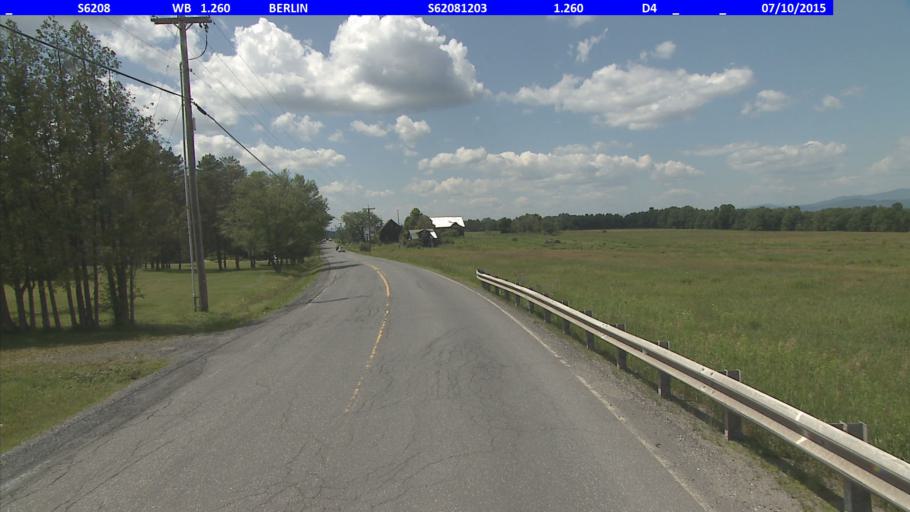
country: US
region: Vermont
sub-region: Washington County
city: Montpelier
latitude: 44.1972
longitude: -72.5665
